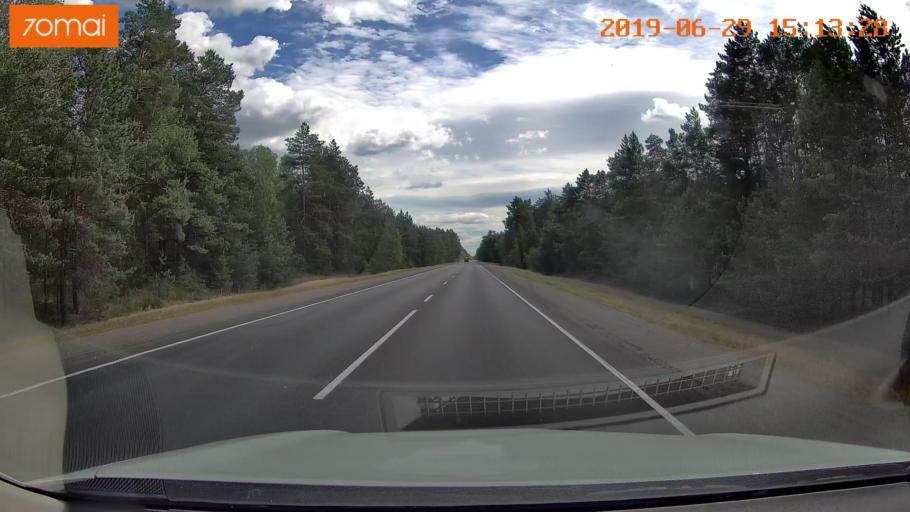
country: BY
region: Brest
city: Mikashevichy
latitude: 52.2774
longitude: 27.4415
